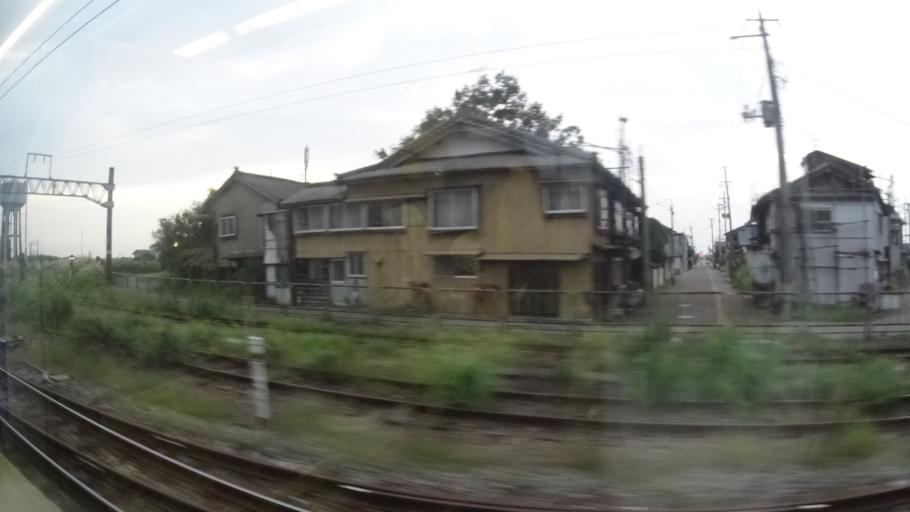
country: JP
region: Niigata
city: Murakami
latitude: 38.1223
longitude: 139.4483
